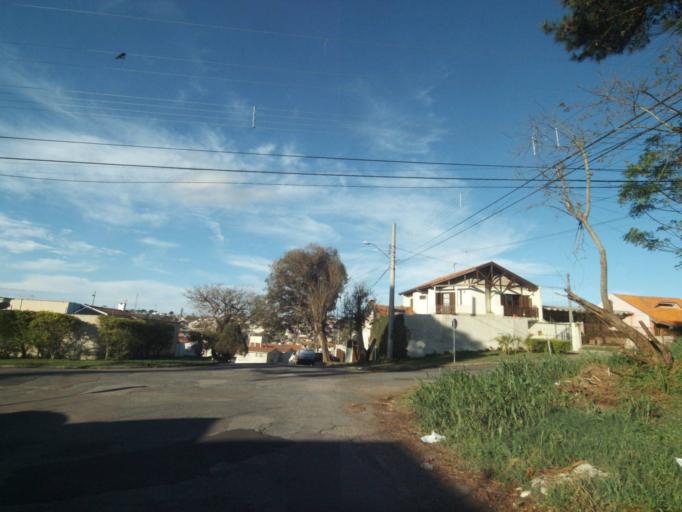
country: BR
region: Parana
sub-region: Curitiba
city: Curitiba
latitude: -25.3821
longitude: -49.2500
